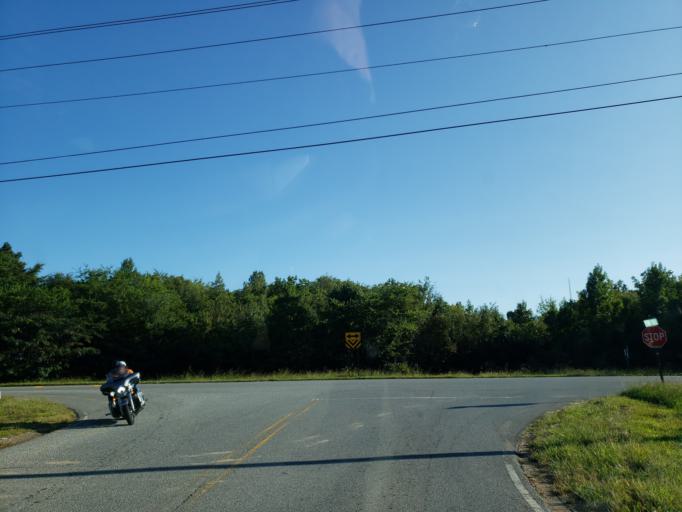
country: US
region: Georgia
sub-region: Bartow County
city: Cartersville
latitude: 34.2729
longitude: -84.8035
